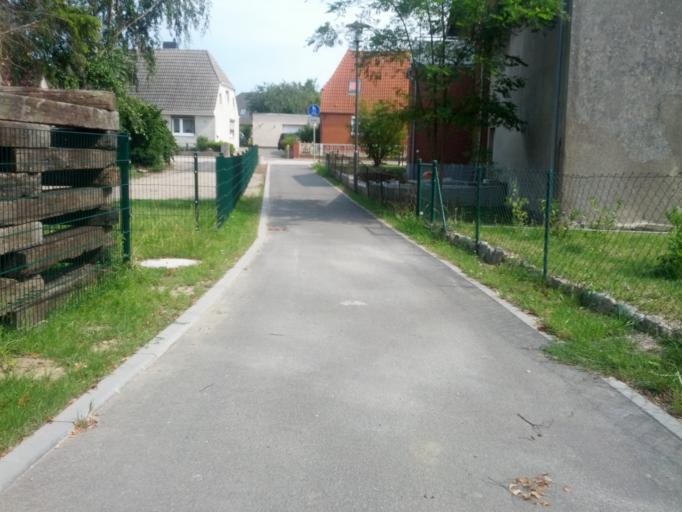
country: DE
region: Mecklenburg-Vorpommern
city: Bastorf
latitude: 54.1416
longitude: 11.7220
